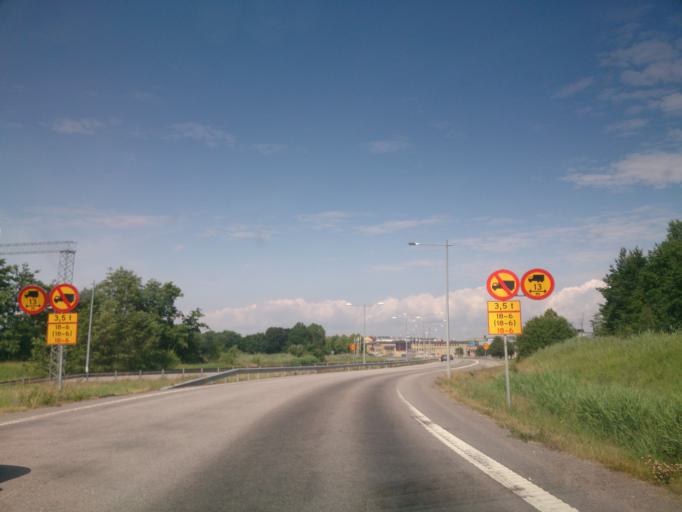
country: SE
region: OEstergoetland
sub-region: Norrkopings Kommun
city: Norrkoping
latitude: 58.5816
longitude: 16.2109
